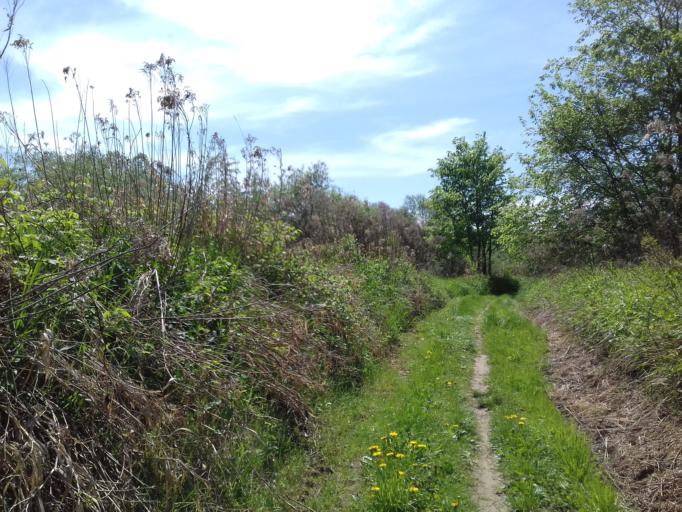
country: PL
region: Lesser Poland Voivodeship
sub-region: Powiat bochenski
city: Stanislawice
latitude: 49.9743
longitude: 20.3431
